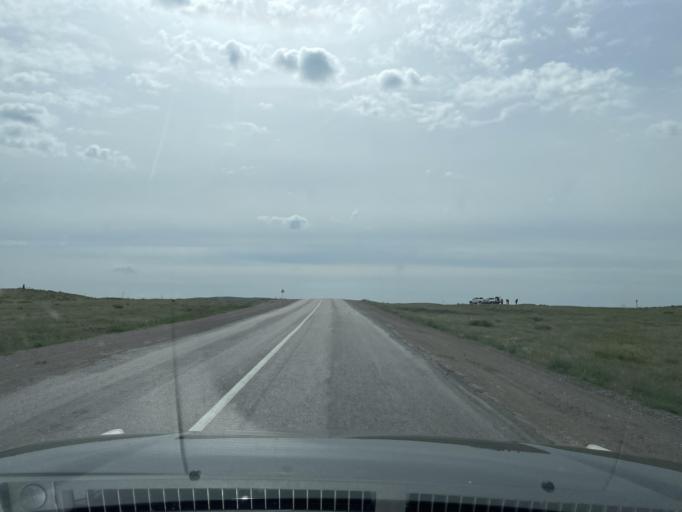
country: KZ
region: Qaraghandy
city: Abay
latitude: 49.5130
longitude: 72.8719
